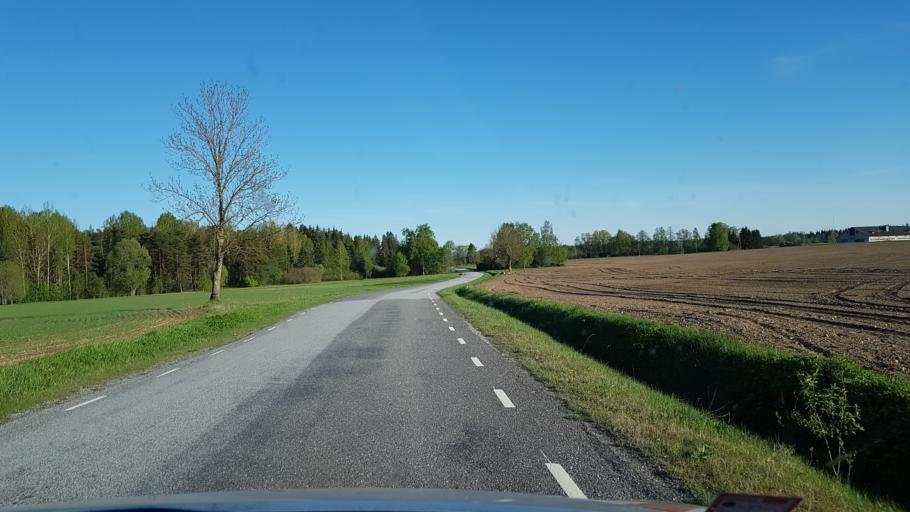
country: EE
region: Vorumaa
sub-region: Voru linn
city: Voru
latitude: 57.9168
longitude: 26.9548
